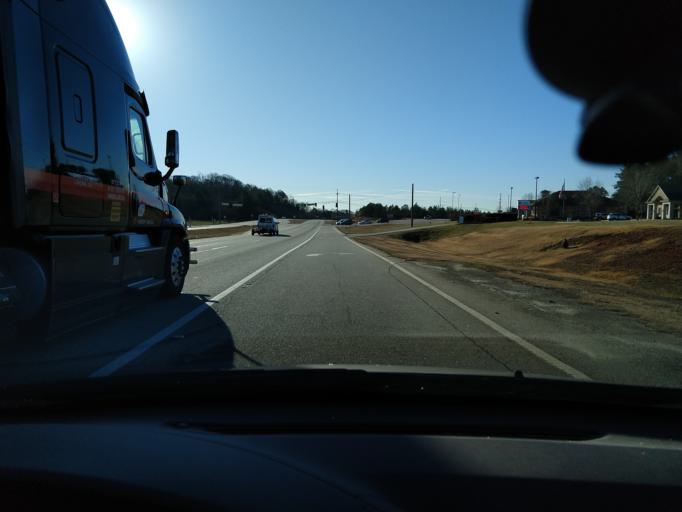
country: US
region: Georgia
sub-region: Jackson County
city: Commerce
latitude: 34.2351
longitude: -83.4533
